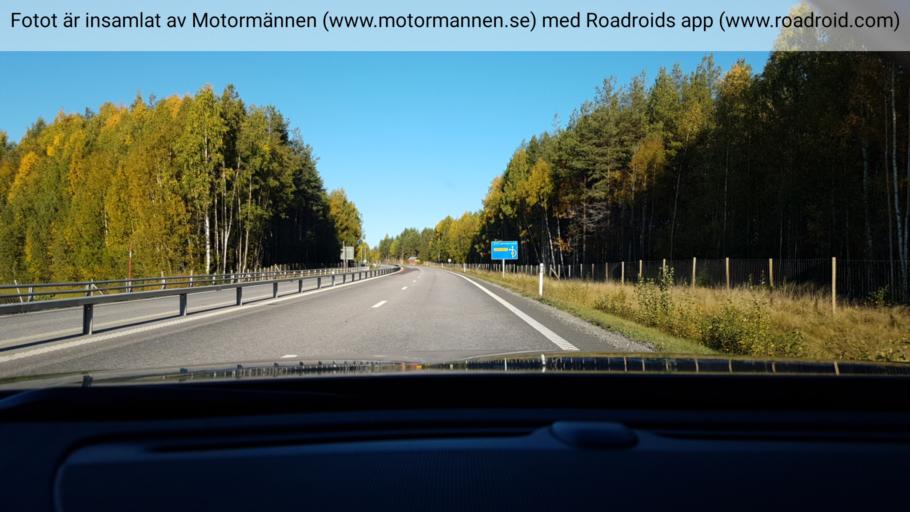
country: SE
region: Norrbotten
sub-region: Pitea Kommun
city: Bergsviken
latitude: 65.3144
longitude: 21.3968
